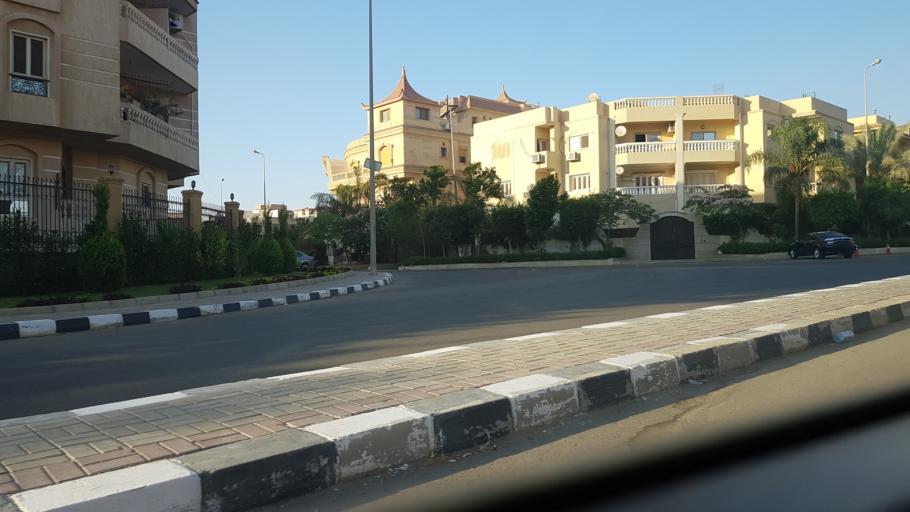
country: EG
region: Muhafazat al Qalyubiyah
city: Al Khankah
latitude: 30.0316
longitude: 31.4403
